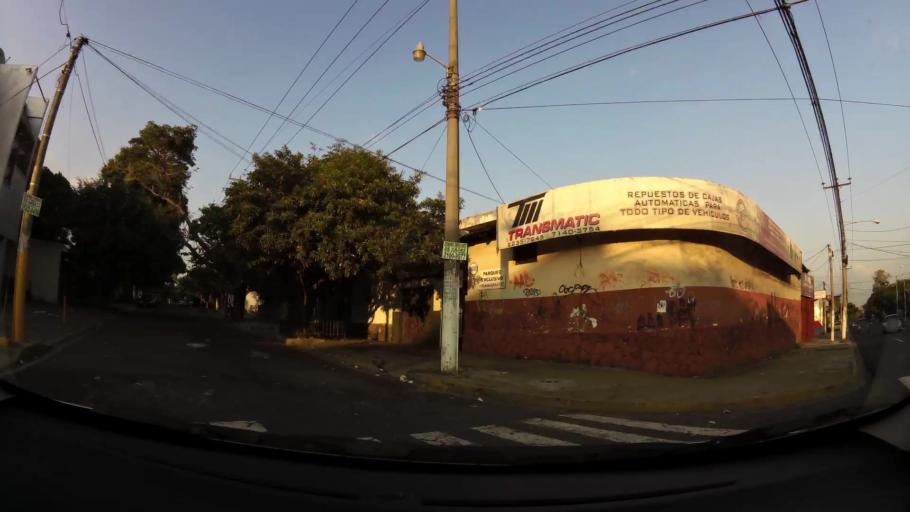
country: SV
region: San Salvador
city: San Salvador
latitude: 13.7140
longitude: -89.1986
